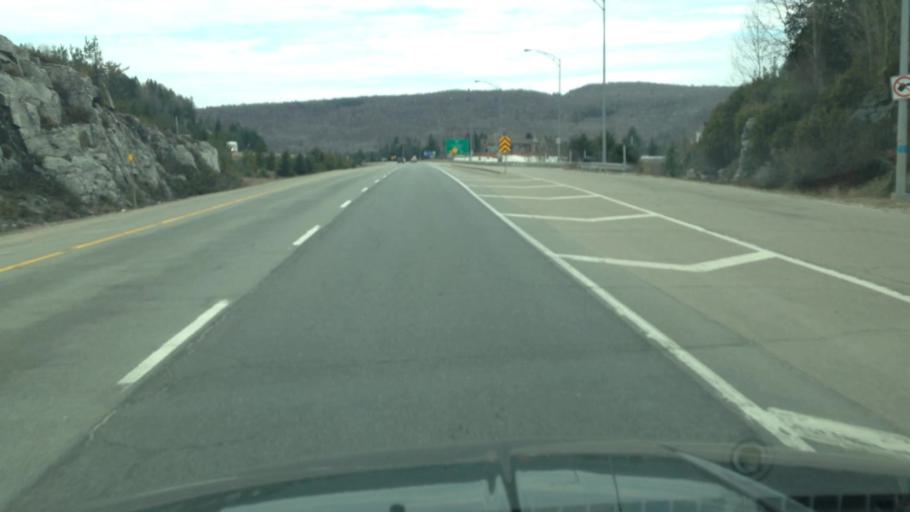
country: CA
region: Quebec
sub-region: Laurentides
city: Mont-Tremblant
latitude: 46.1152
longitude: -74.5856
